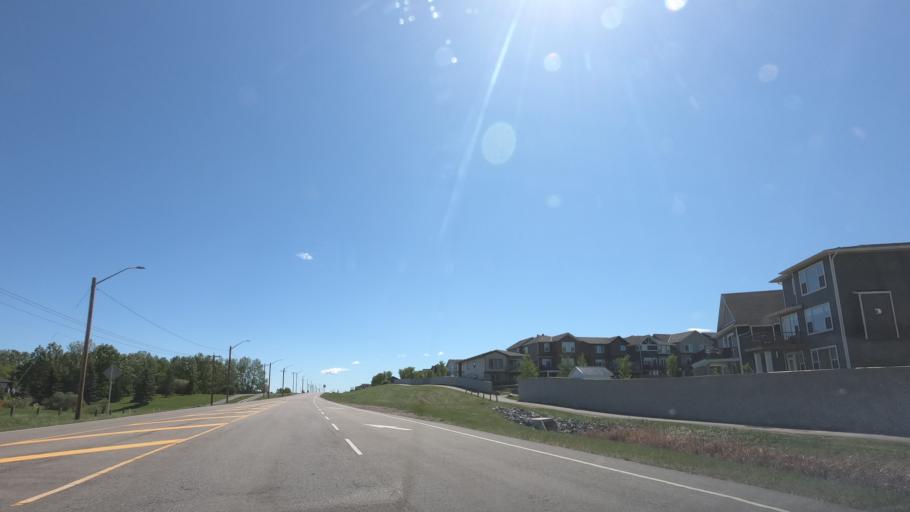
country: CA
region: Alberta
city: Airdrie
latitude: 51.2707
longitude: -113.9793
